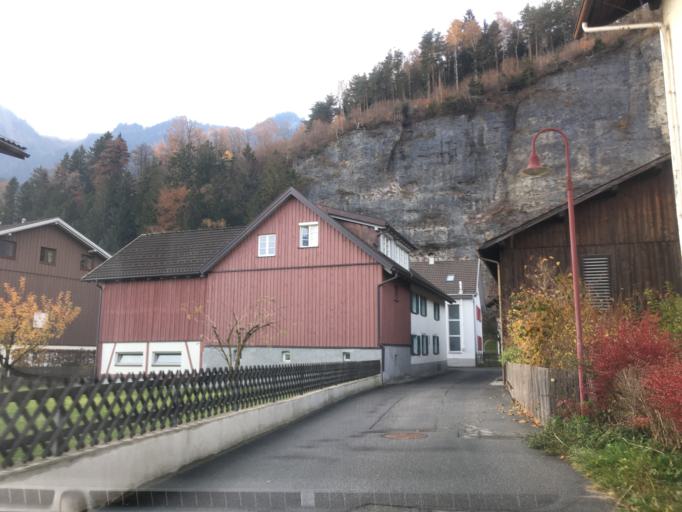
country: AT
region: Vorarlberg
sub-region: Politischer Bezirk Bludenz
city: Buers
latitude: 47.1493
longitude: 9.8034
